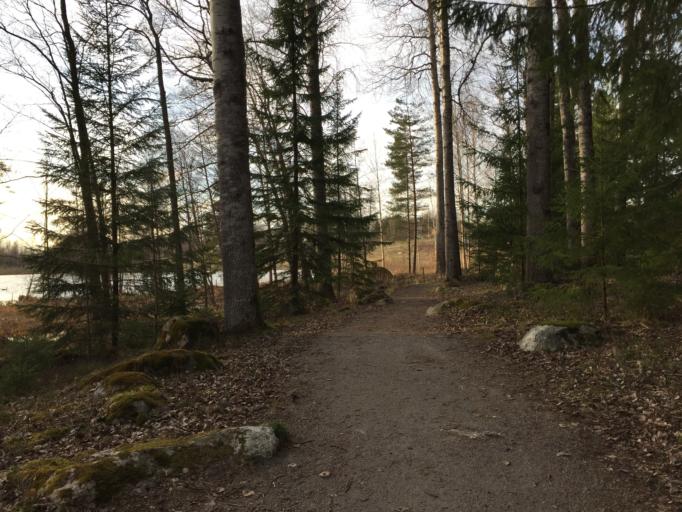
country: SE
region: Soedermanland
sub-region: Katrineholms Kommun
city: Katrineholm
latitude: 58.9756
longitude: 16.1995
